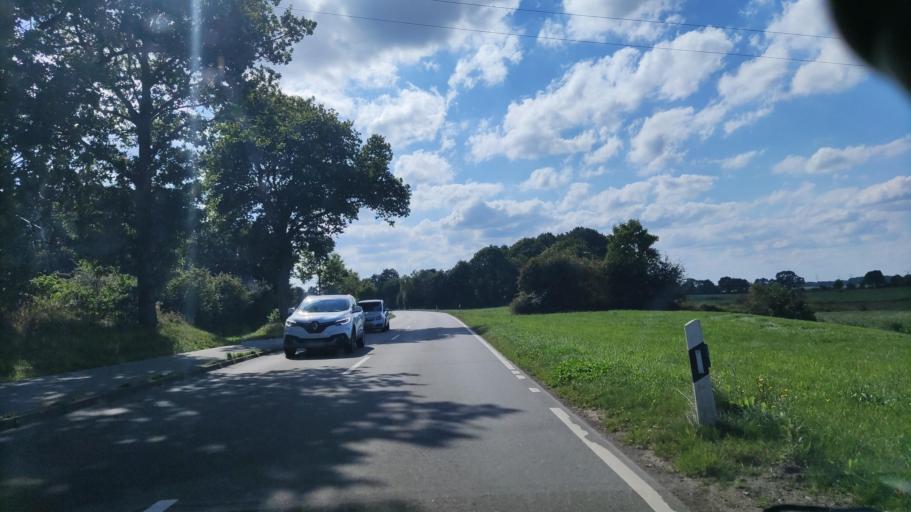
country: DE
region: Schleswig-Holstein
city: Neu Duvenstedt
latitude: 54.3697
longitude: 9.6608
